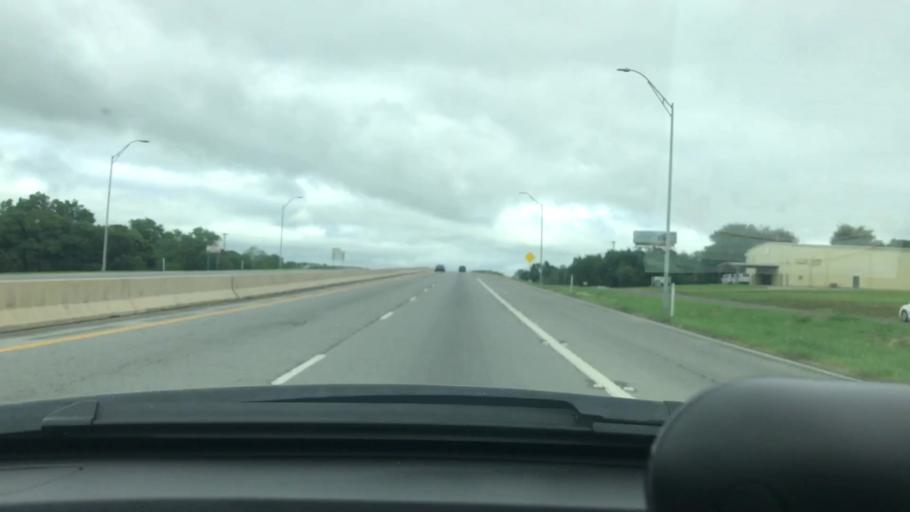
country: US
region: Texas
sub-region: Grayson County
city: Sherman
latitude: 33.6262
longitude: -96.6128
